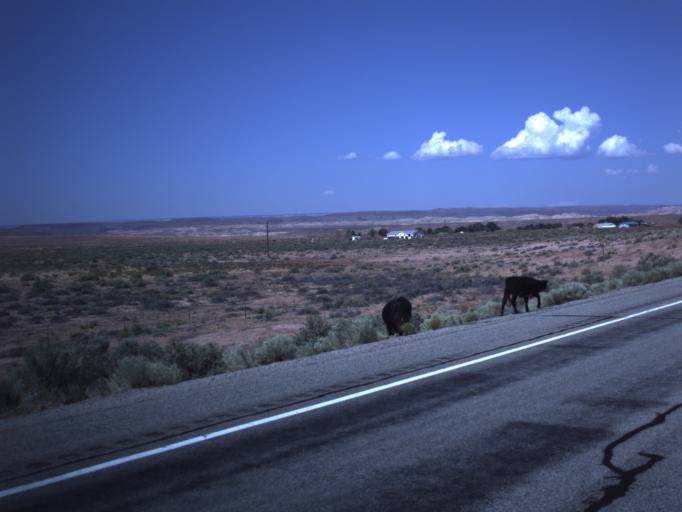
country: US
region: Utah
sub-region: San Juan County
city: Blanding
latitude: 37.2087
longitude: -109.6091
